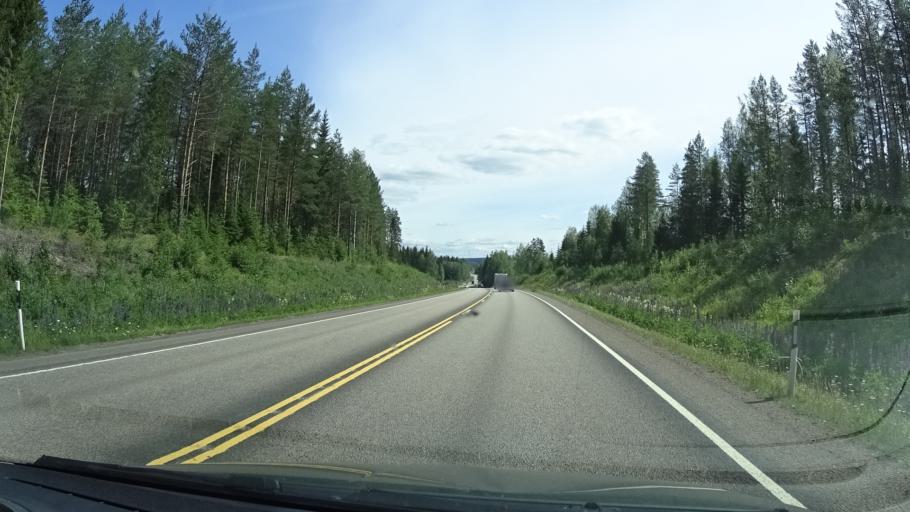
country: FI
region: Central Finland
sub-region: Jyvaeskylae
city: Uurainen
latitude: 62.2670
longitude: 25.4333
